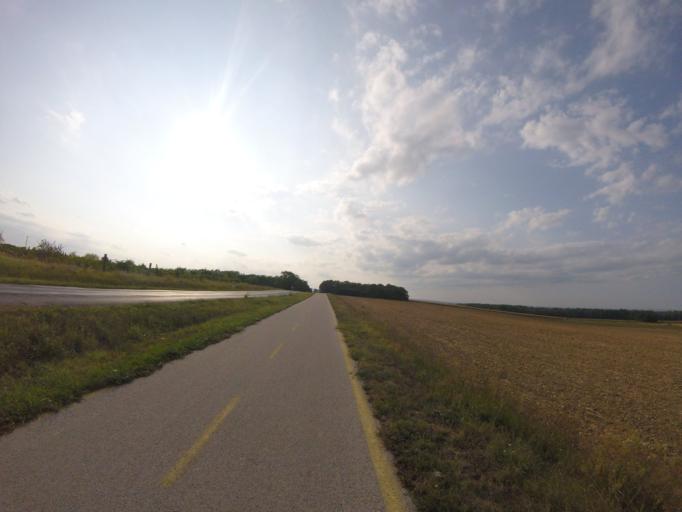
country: HU
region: Gyor-Moson-Sopron
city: Fertod
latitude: 47.6160
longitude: 16.8223
